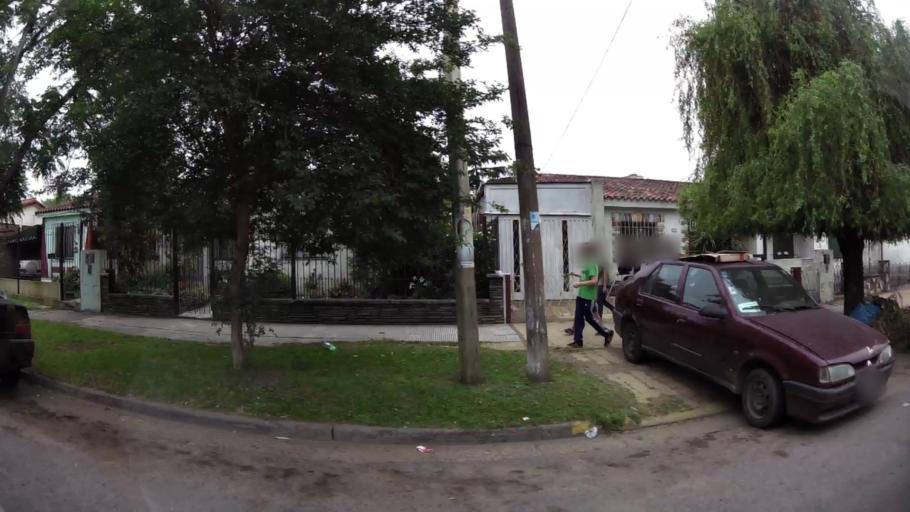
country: AR
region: Buenos Aires
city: San Justo
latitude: -34.7153
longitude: -58.5399
